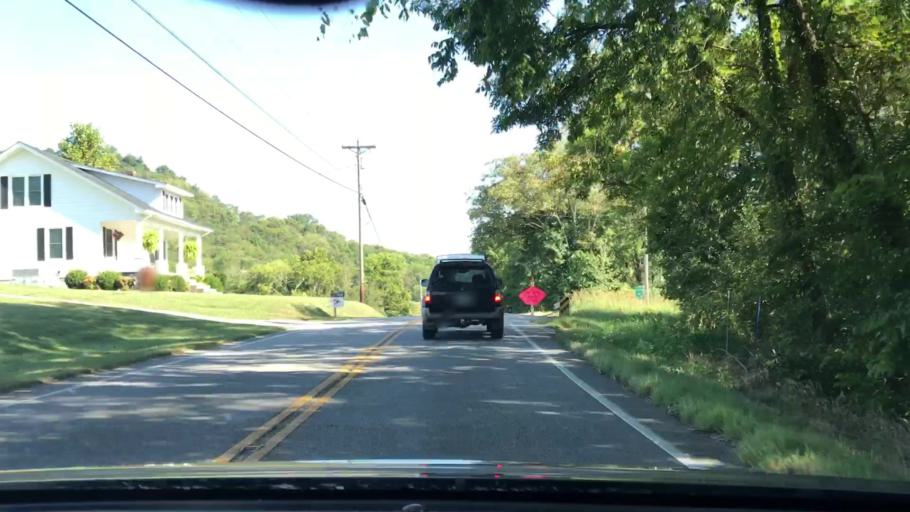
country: US
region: Tennessee
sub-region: Smith County
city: Carthage
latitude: 36.3447
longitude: -85.8978
